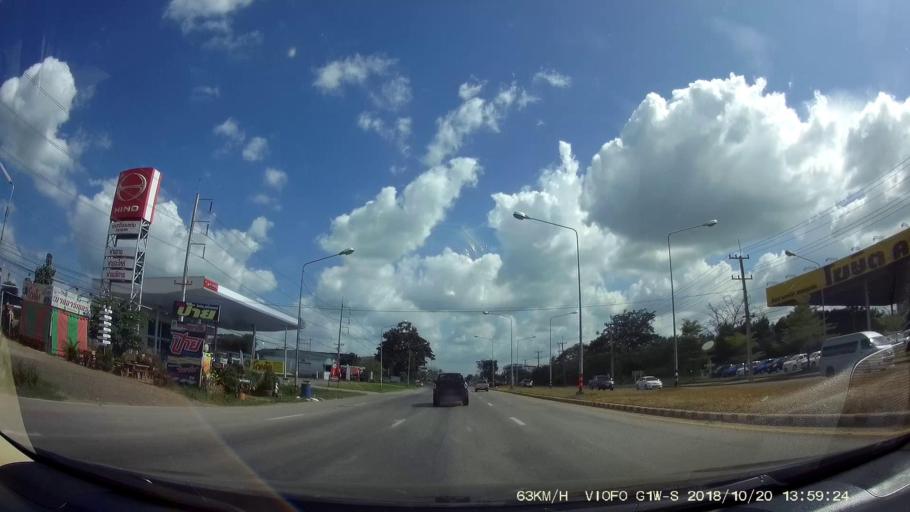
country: TH
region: Khon Kaen
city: Chum Phae
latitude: 16.5248
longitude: 102.1125
